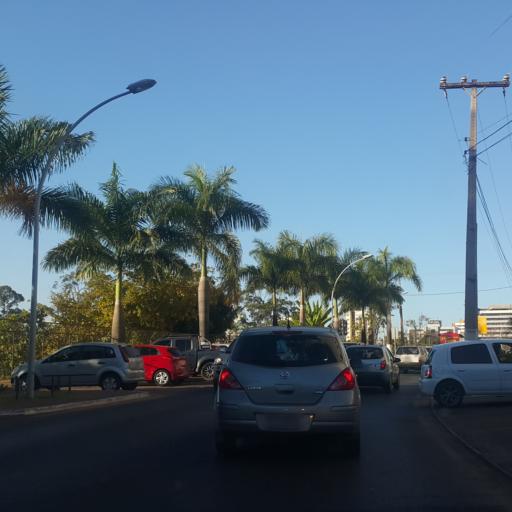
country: BR
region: Federal District
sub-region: Brasilia
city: Brasilia
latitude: -15.8340
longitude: -48.0212
